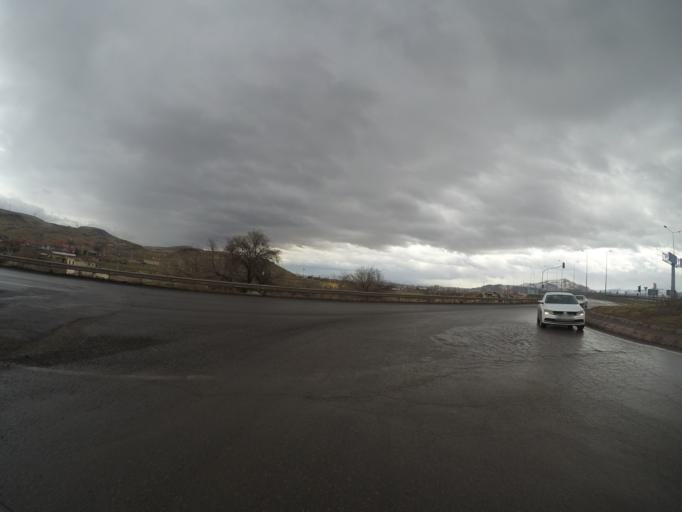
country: TR
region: Kayseri
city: Melikgazi
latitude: 38.7519
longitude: 35.3108
